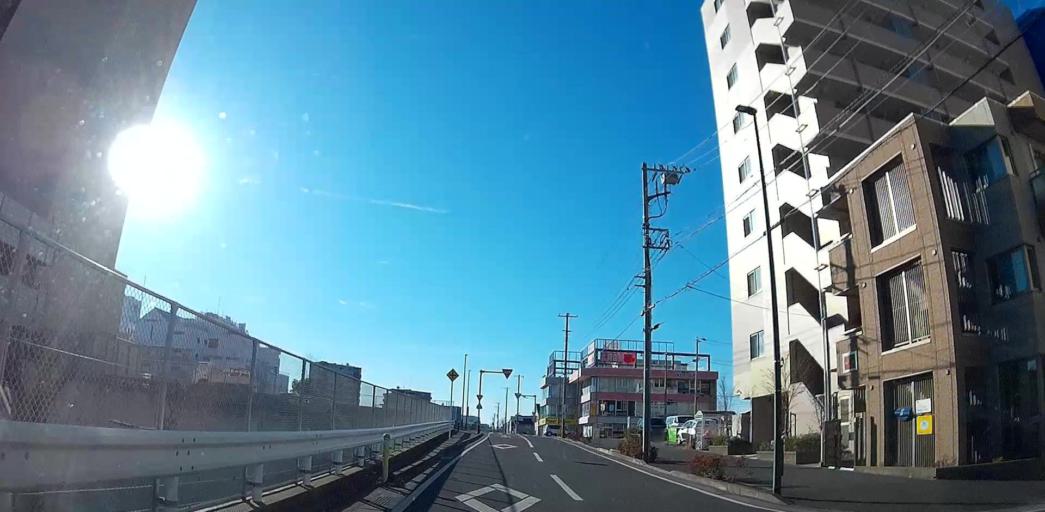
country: JP
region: Chiba
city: Shiroi
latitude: 35.7780
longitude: 139.9995
